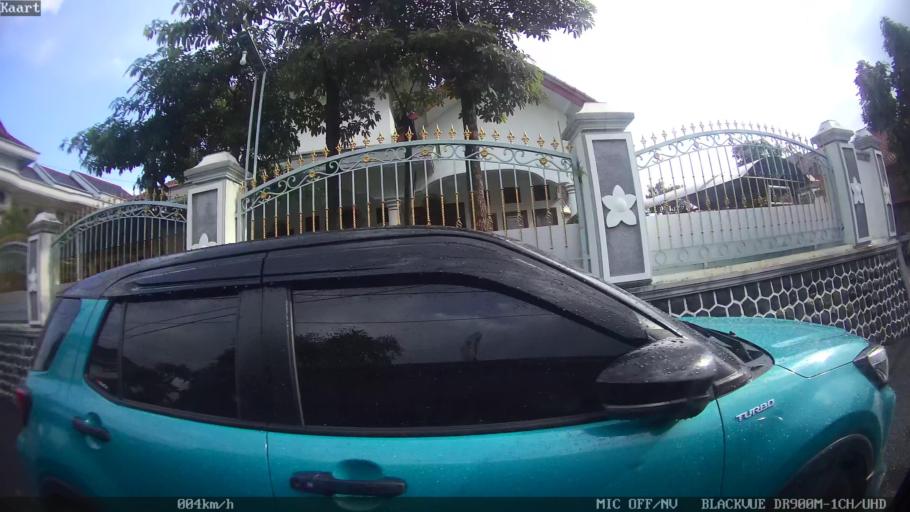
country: ID
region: Lampung
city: Kedaton
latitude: -5.3874
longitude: 105.2997
